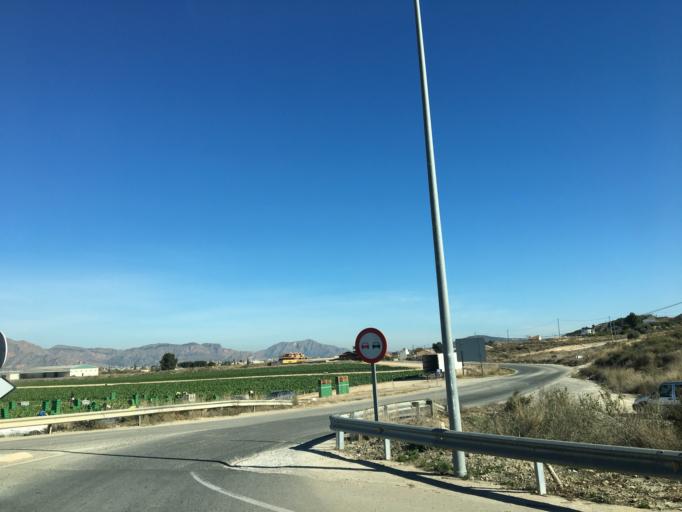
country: ES
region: Murcia
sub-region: Murcia
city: Beniel
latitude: 38.0032
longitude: -1.0111
